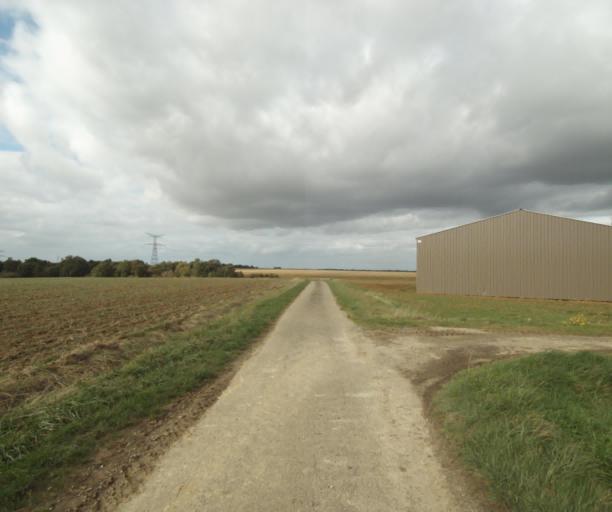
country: FR
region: Midi-Pyrenees
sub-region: Departement du Tarn-et-Garonne
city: Finhan
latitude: 43.9051
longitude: 1.1040
